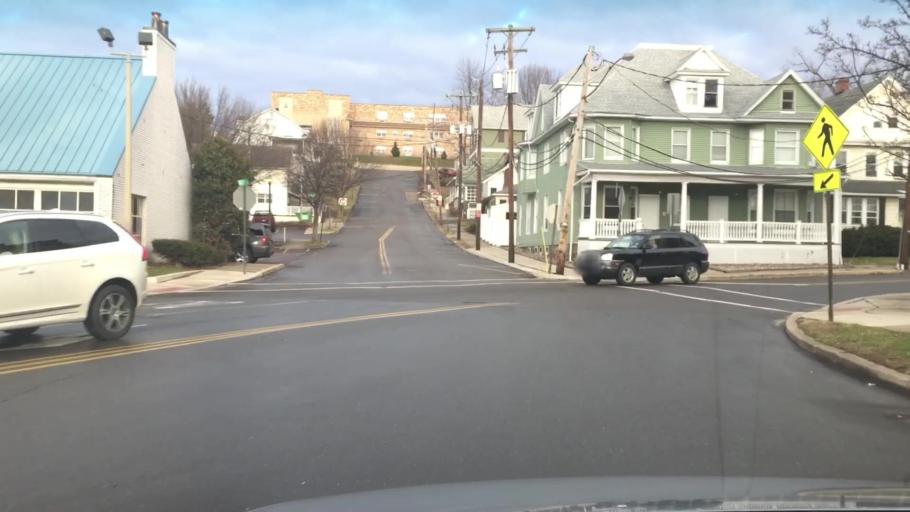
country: US
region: Pennsylvania
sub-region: Columbia County
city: Bloomsburg
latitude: 41.0046
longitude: -76.4537
